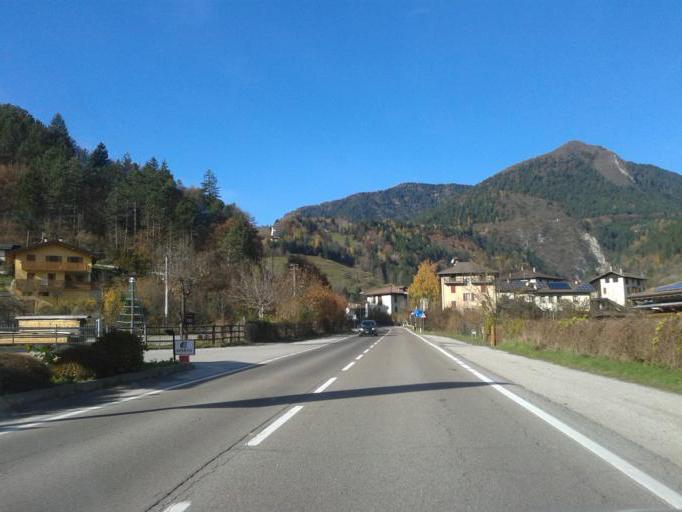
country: IT
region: Trentino-Alto Adige
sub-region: Provincia di Trento
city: Pieve di Ledro
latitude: 45.8926
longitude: 10.6856
